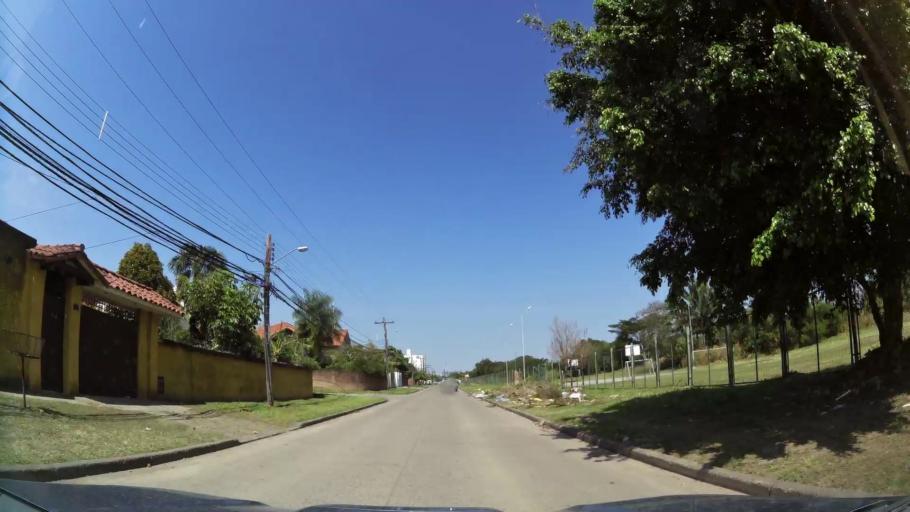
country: BO
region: Santa Cruz
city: Santa Cruz de la Sierra
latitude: -17.7459
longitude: -63.1696
